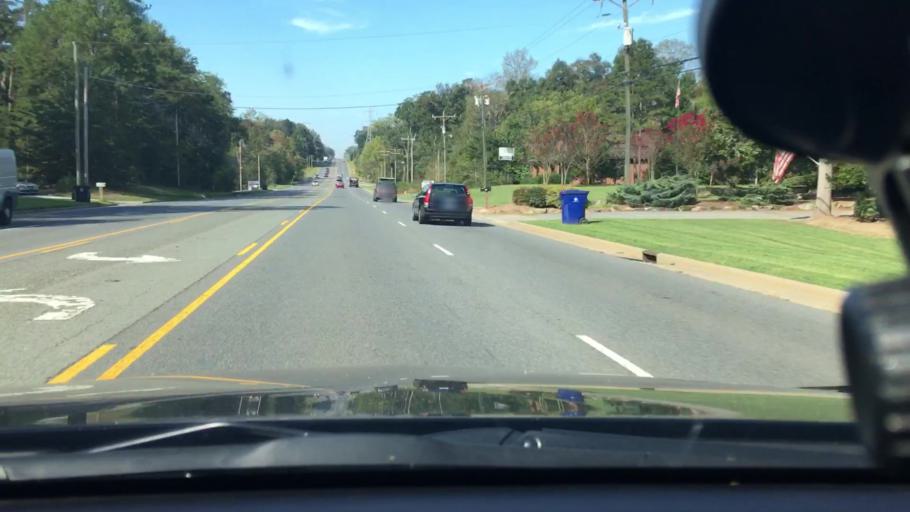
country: US
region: North Carolina
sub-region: Cabarrus County
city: Midland
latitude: 35.2499
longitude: -80.5188
